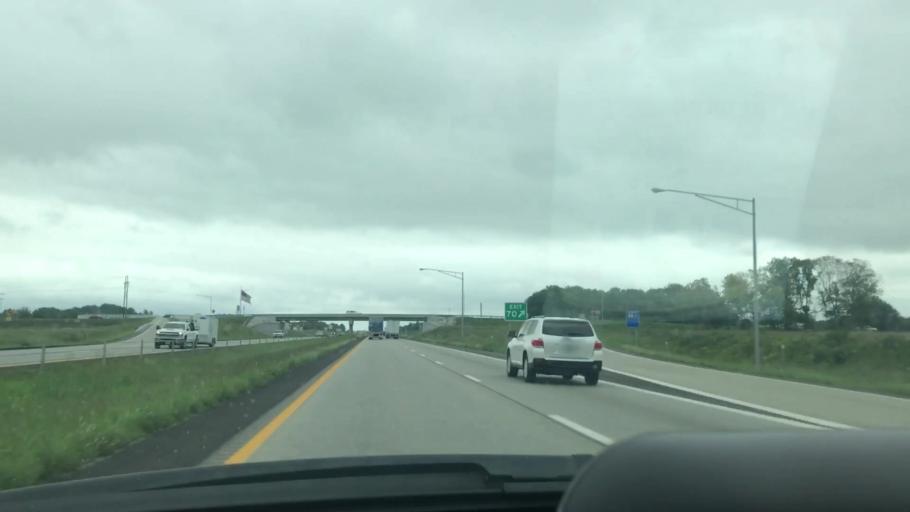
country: US
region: Missouri
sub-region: Greene County
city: Republic
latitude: 37.1999
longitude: -93.4261
